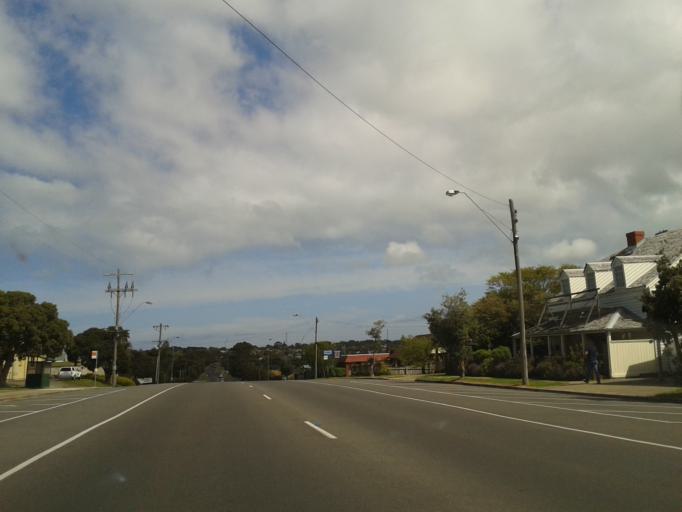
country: AU
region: Victoria
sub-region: Glenelg
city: Portland
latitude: -38.3512
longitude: 141.6062
